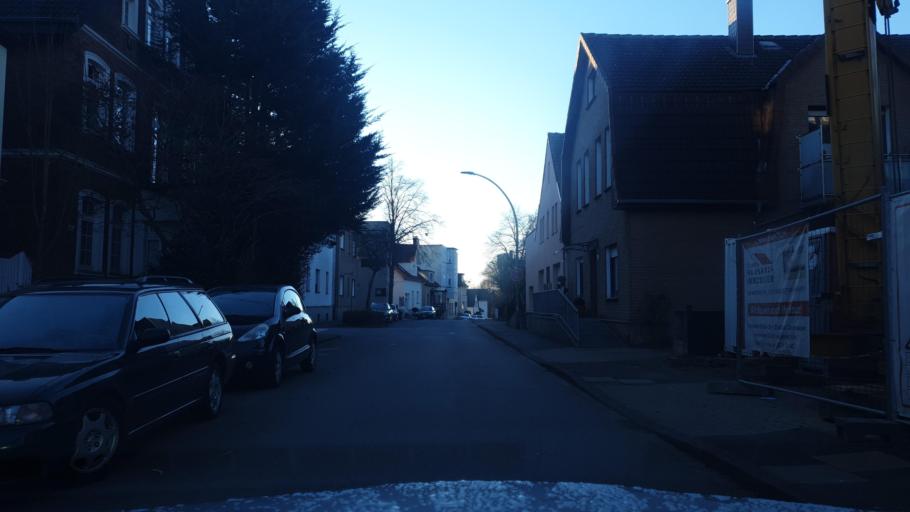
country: DE
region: North Rhine-Westphalia
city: Bad Oeynhausen
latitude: 52.2029
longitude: 8.7875
